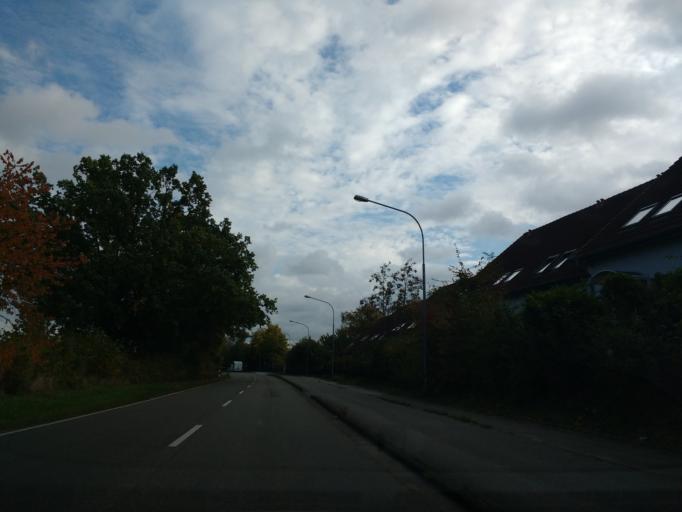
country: DE
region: Schleswig-Holstein
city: Travemuende
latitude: 53.9696
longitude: 10.8594
